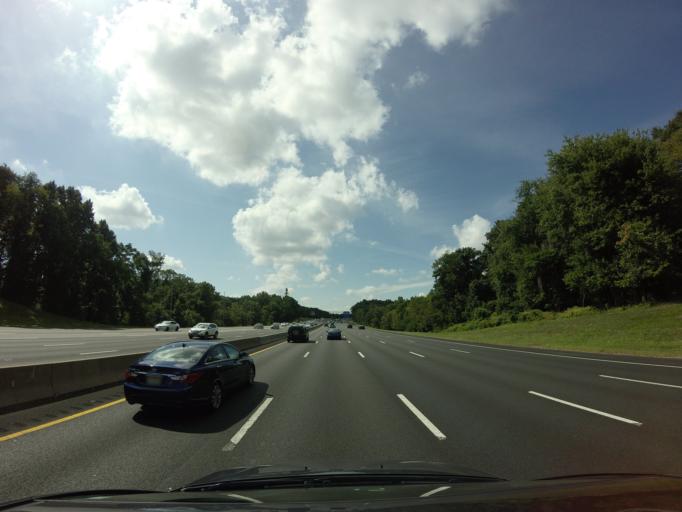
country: US
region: New Jersey
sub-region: Union County
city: Clark
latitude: 40.6135
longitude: -74.3118
